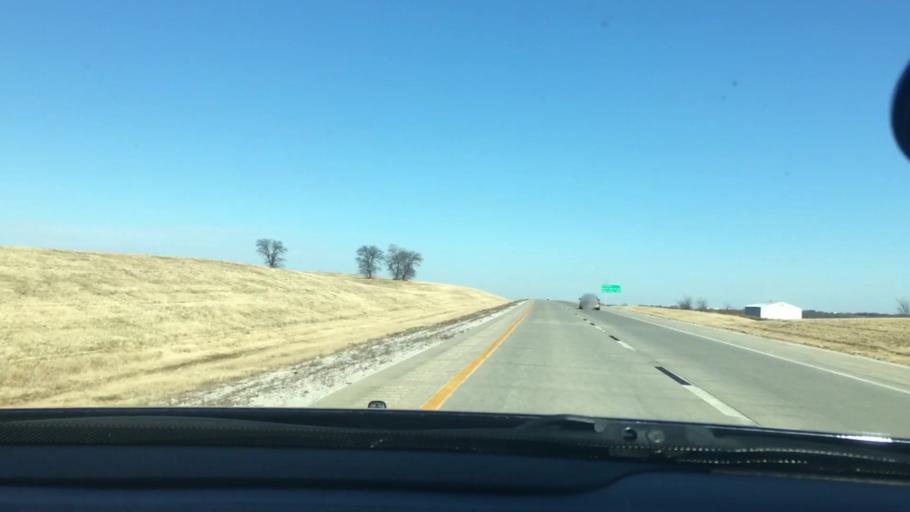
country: US
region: Oklahoma
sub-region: Carter County
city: Ardmore
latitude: 34.0823
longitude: -97.1497
